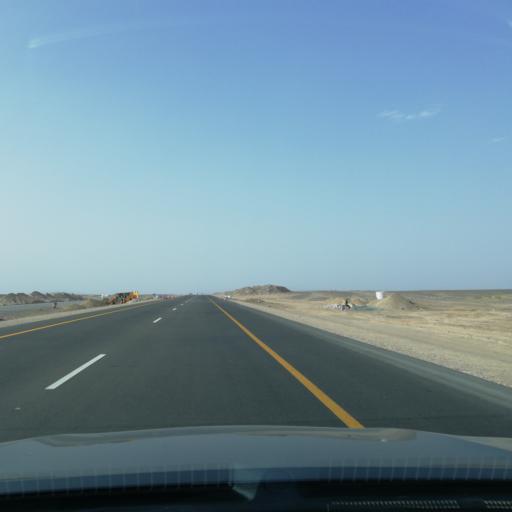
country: OM
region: Muhafazat ad Dakhiliyah
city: Adam
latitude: 22.1712
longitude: 57.5216
